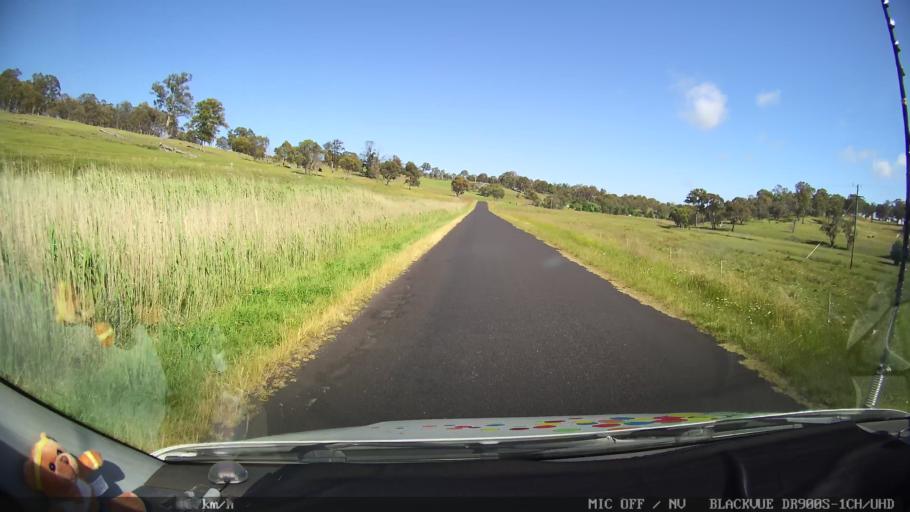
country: AU
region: New South Wales
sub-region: Guyra
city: Guyra
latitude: -30.1162
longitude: 151.6867
